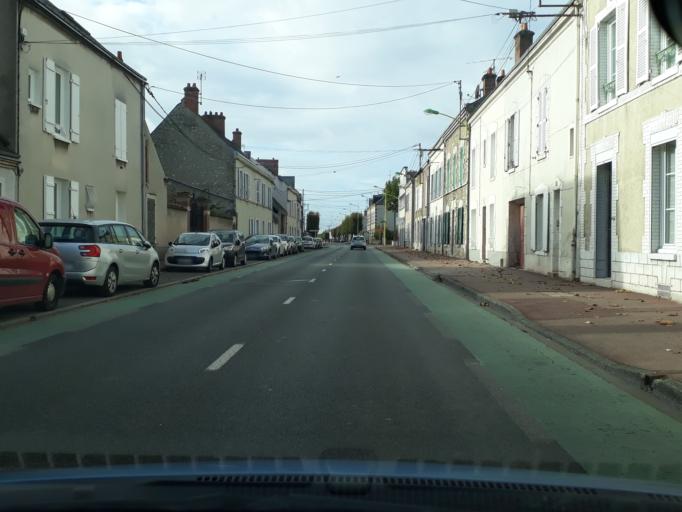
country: FR
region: Centre
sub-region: Departement du Loiret
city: Pithiviers
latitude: 48.1705
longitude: 2.2532
